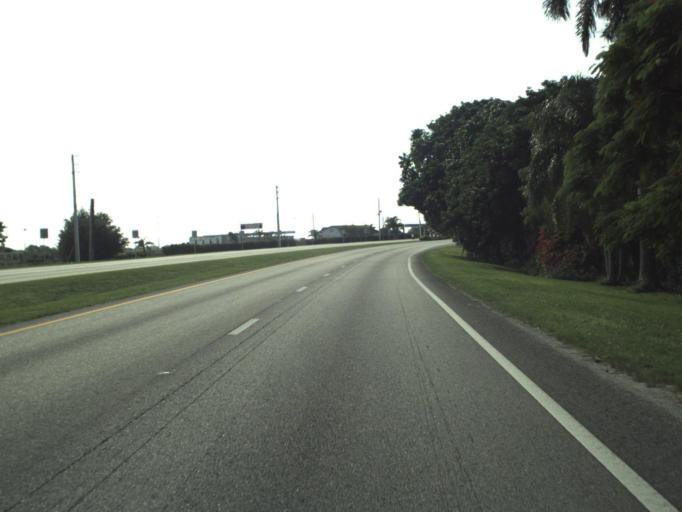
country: US
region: Florida
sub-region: Palm Beach County
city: South Bay
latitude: 26.6777
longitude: -80.7256
